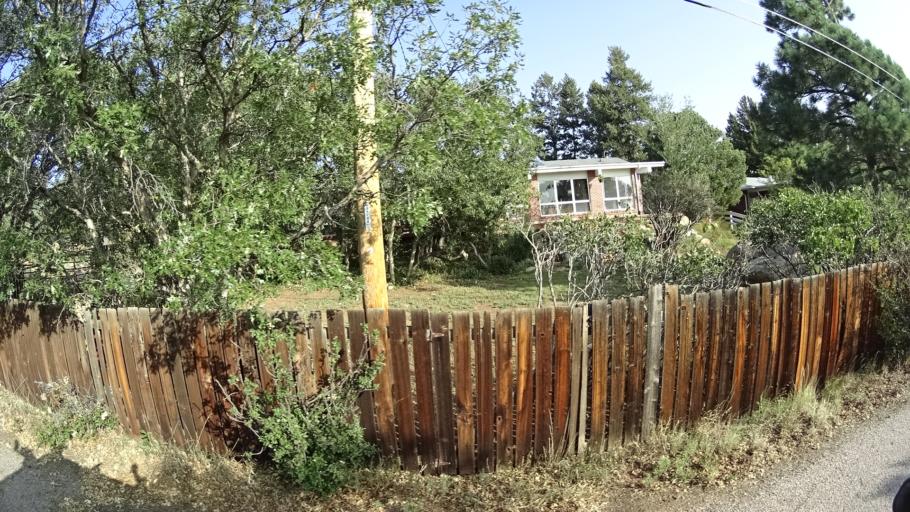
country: US
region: Colorado
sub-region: El Paso County
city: Colorado Springs
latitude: 38.8141
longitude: -104.8555
